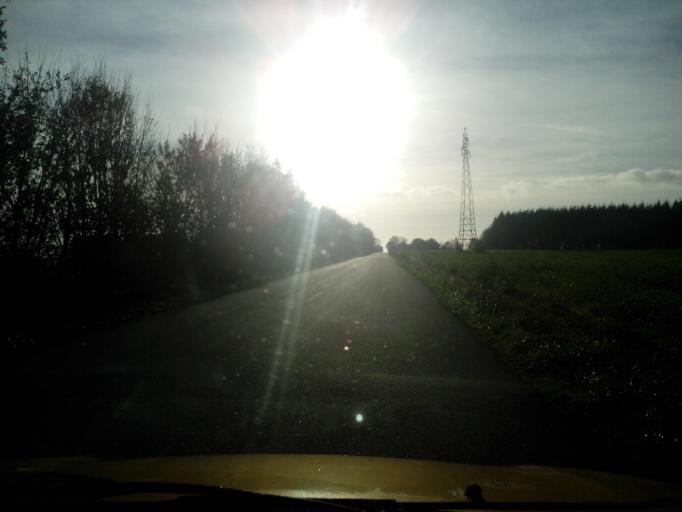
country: FR
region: Brittany
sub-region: Departement du Morbihan
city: Meneac
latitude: 48.0843
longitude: -2.4456
